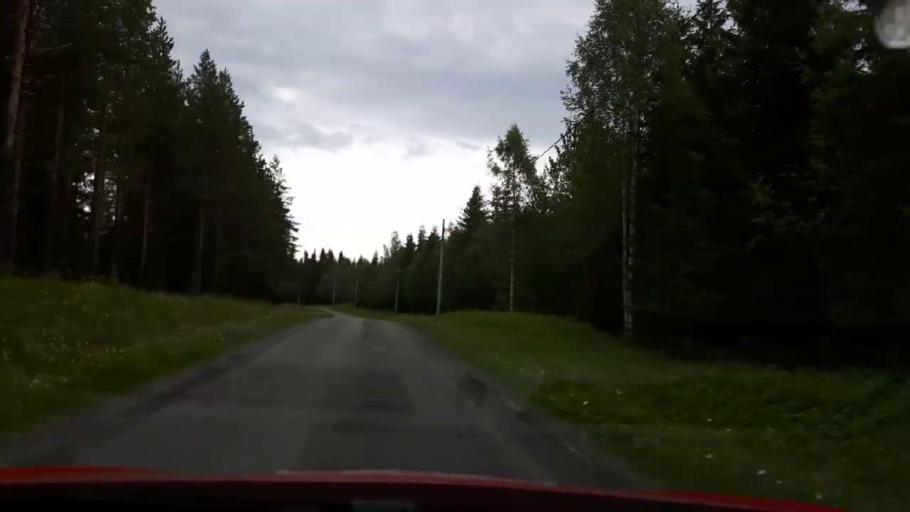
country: SE
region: Jaemtland
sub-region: OEstersunds Kommun
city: Lit
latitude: 63.3740
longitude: 15.1043
